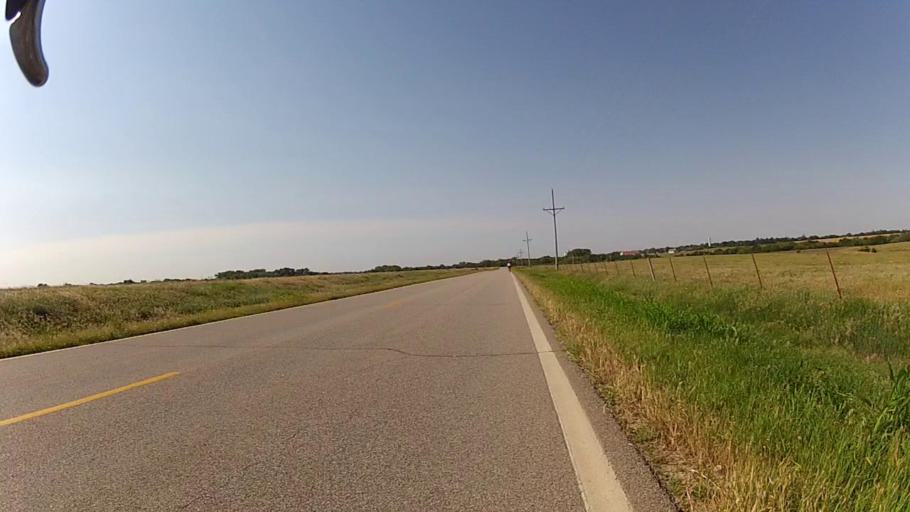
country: US
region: Kansas
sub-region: Sumner County
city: Caldwell
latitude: 37.0515
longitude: -97.6007
